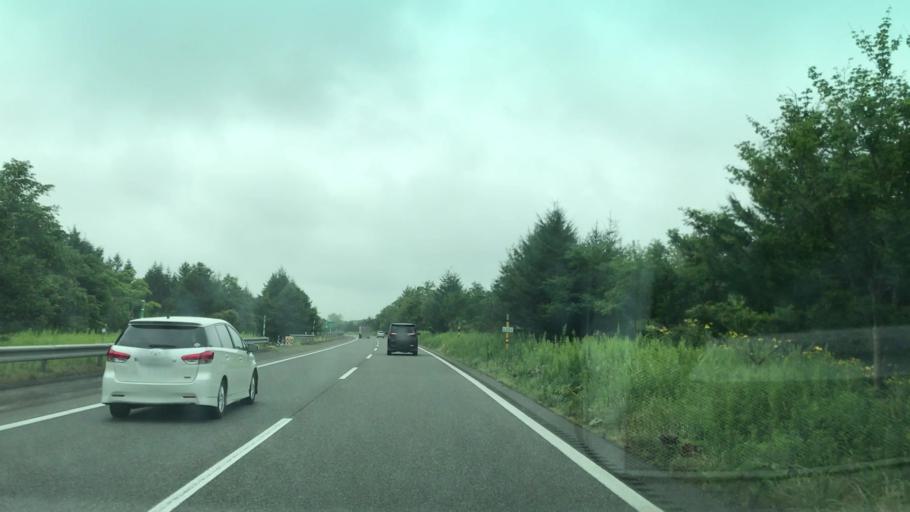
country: JP
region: Hokkaido
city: Chitose
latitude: 42.7868
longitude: 141.6264
